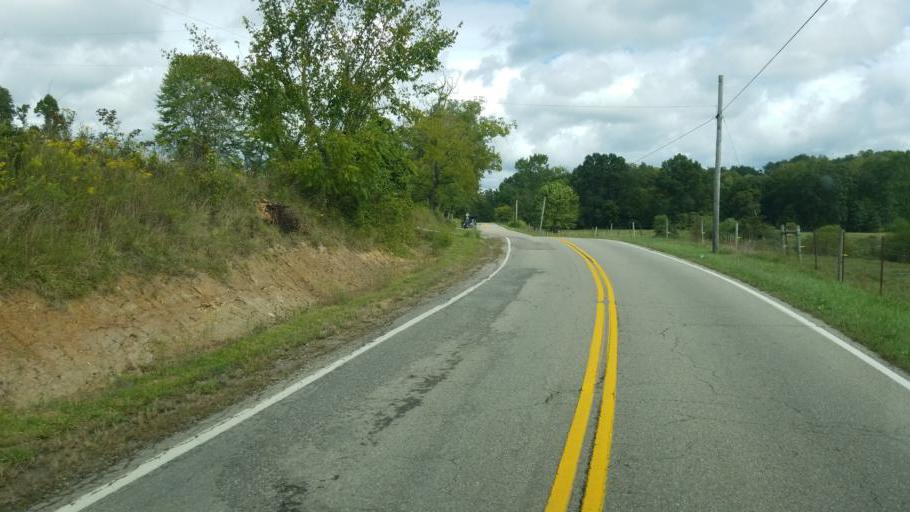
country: US
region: Ohio
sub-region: Jackson County
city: Oak Hill
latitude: 38.9049
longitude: -82.6321
